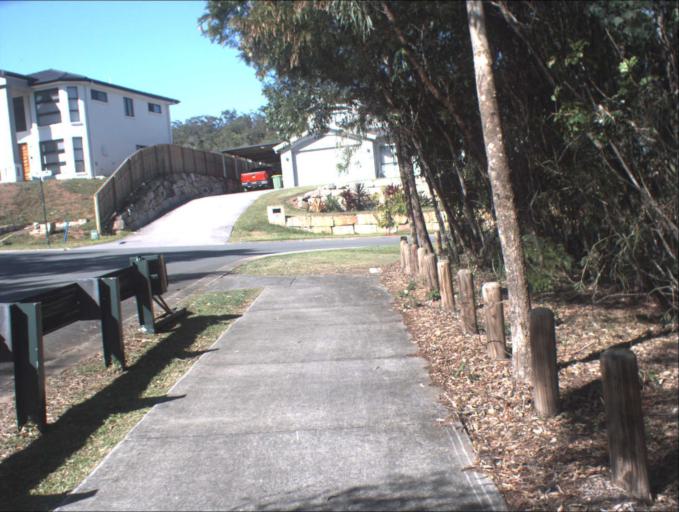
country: AU
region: Queensland
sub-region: Logan
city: Slacks Creek
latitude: -27.6327
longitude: 153.1588
